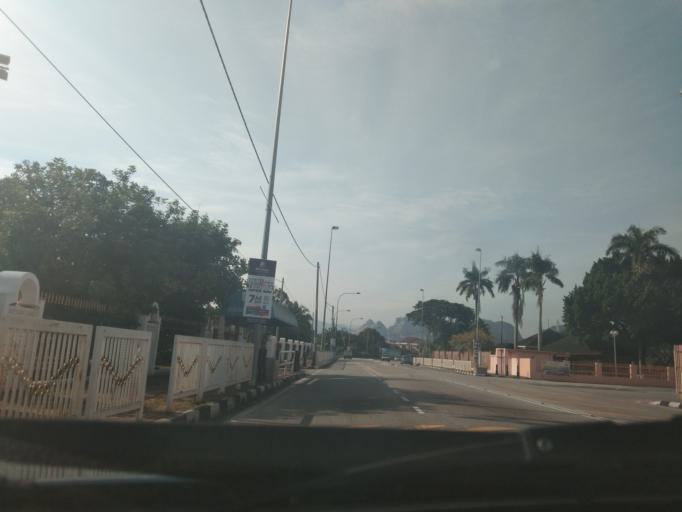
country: MY
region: Perak
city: Ipoh
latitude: 4.5893
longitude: 101.1262
